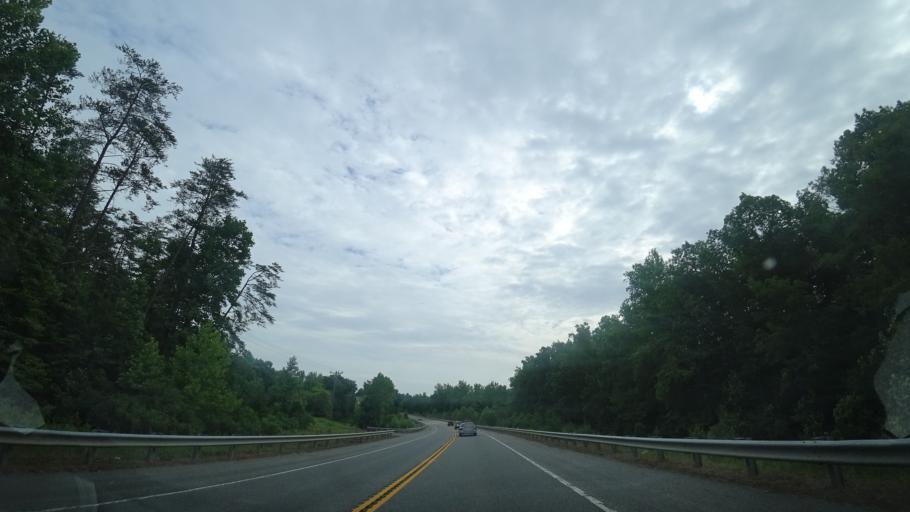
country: US
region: Virginia
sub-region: Spotsylvania County
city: Spotsylvania Courthouse
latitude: 38.1777
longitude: -77.6256
